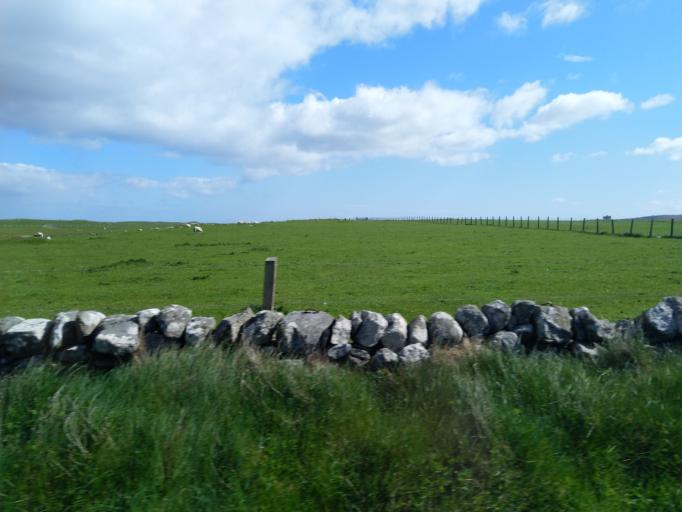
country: GB
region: Scotland
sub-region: Eilean Siar
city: Barra
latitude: 56.4839
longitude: -6.9051
